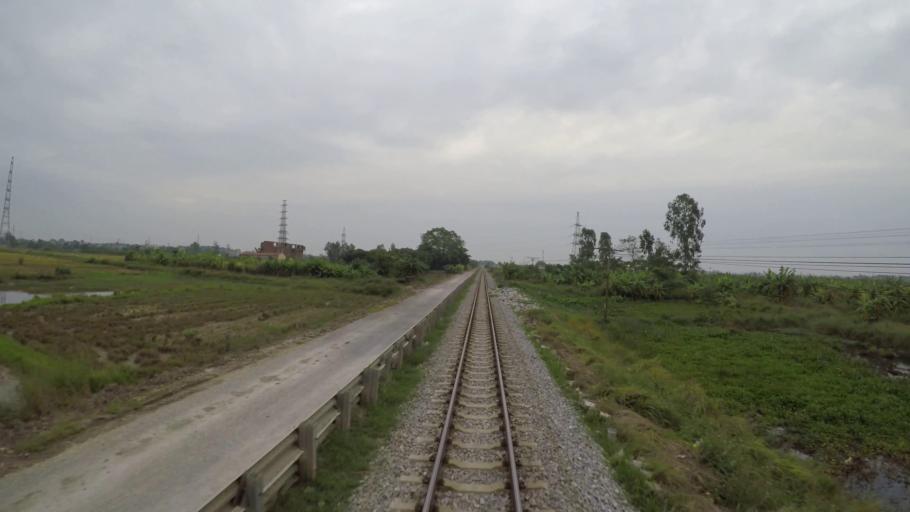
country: VN
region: Hai Duong
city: Ke Sat
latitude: 20.9657
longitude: 106.1242
